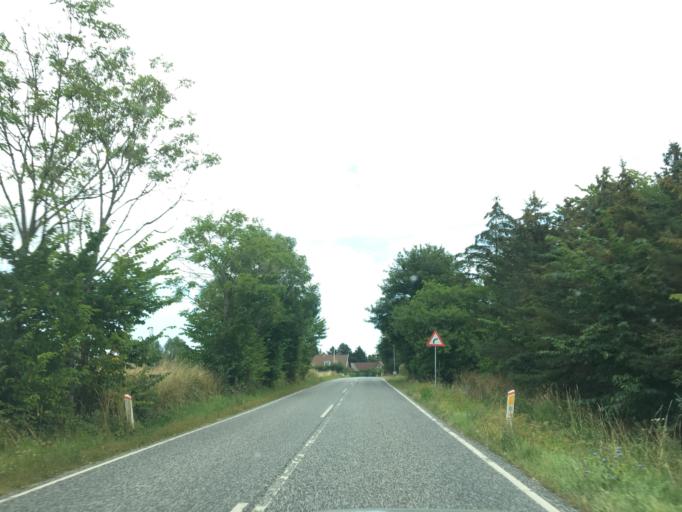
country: DK
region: South Denmark
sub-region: Nyborg Kommune
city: Ullerslev
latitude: 55.3189
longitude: 10.6844
